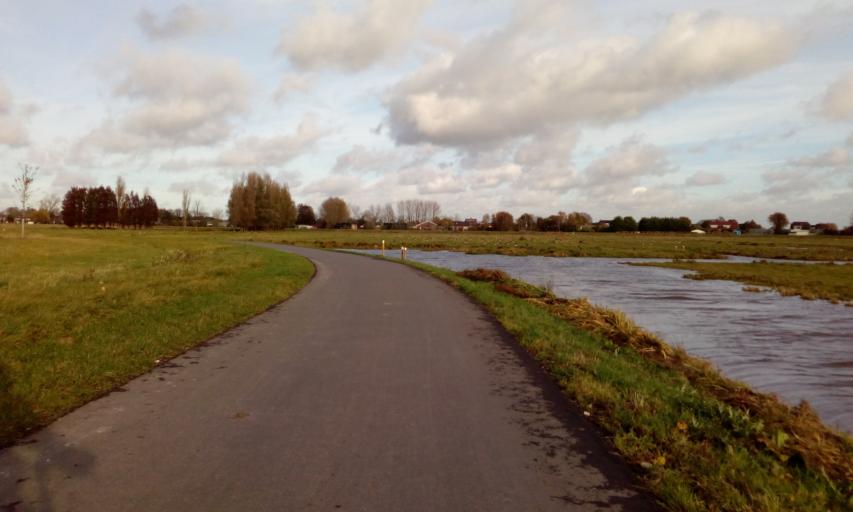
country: NL
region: South Holland
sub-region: Gemeente Lansingerland
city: Berkel en Rodenrijs
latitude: 52.0183
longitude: 4.4757
